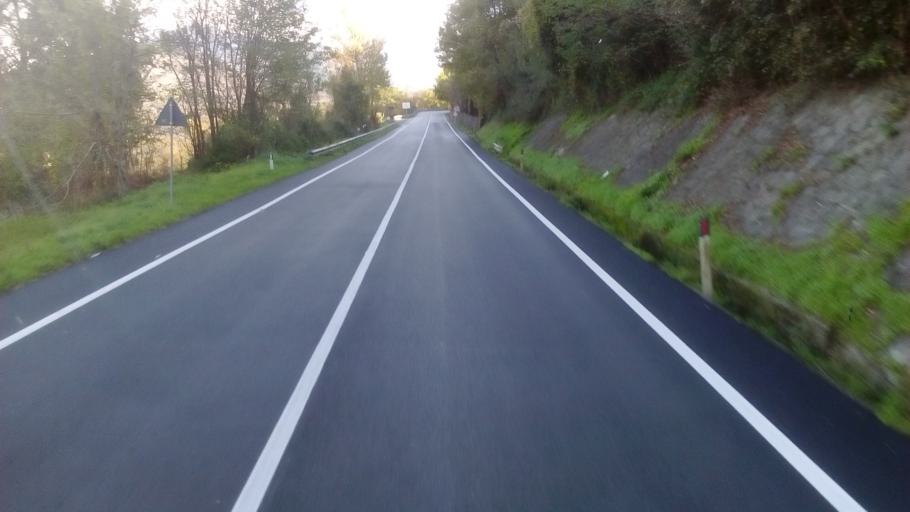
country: IT
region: Molise
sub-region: Provincia di Isernia
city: Conca Casale
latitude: 41.4578
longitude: 14.0126
